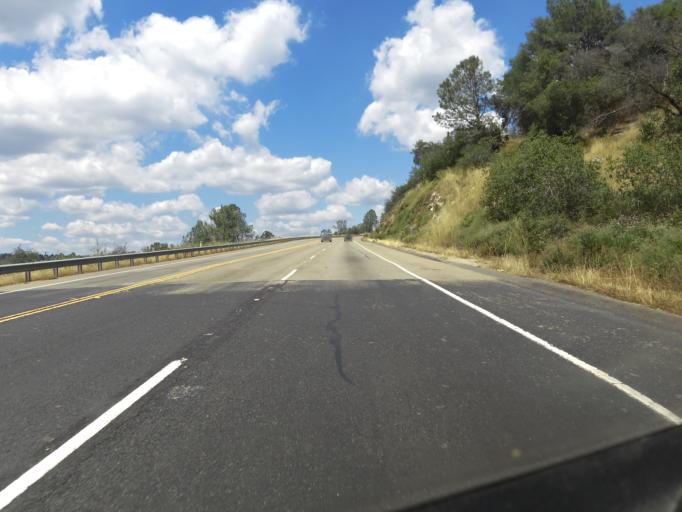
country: US
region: California
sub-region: Madera County
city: Yosemite Lakes
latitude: 37.1982
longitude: -119.7223
